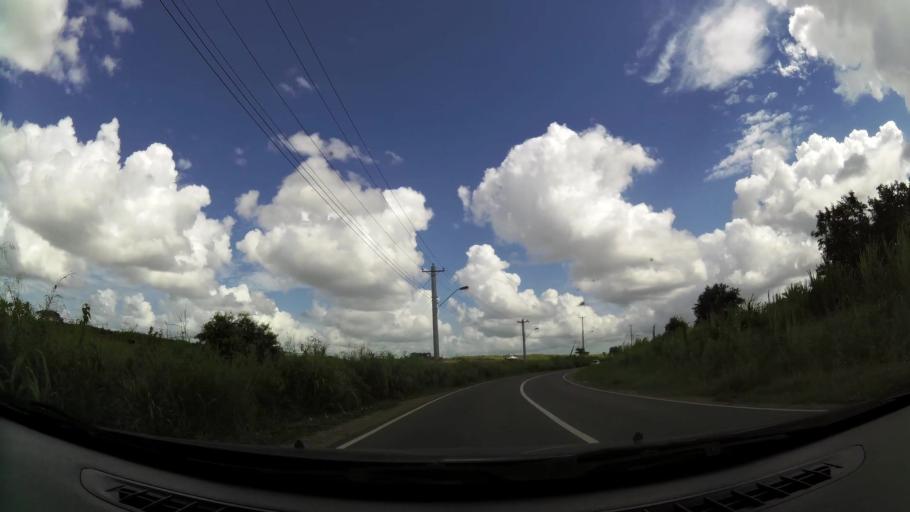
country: TT
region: Penal/Debe
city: Debe
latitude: 10.2311
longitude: -61.4818
